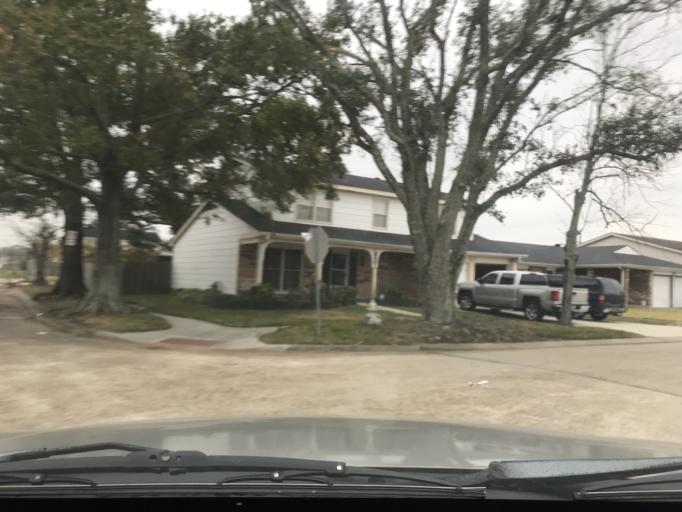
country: US
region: Louisiana
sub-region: Jefferson Parish
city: Woodmere
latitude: 29.8612
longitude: -90.0748
